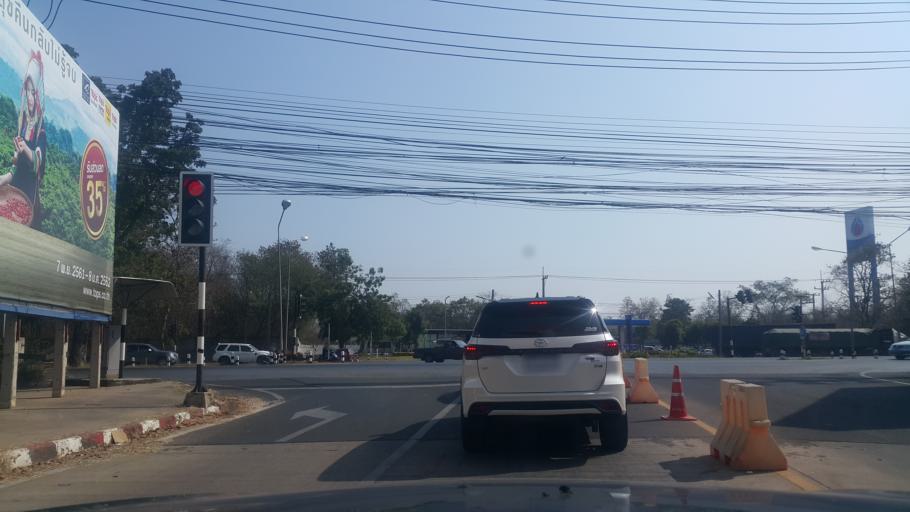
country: TH
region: Nakhon Ratchasima
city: Nakhon Ratchasima
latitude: 14.9311
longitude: 102.0556
